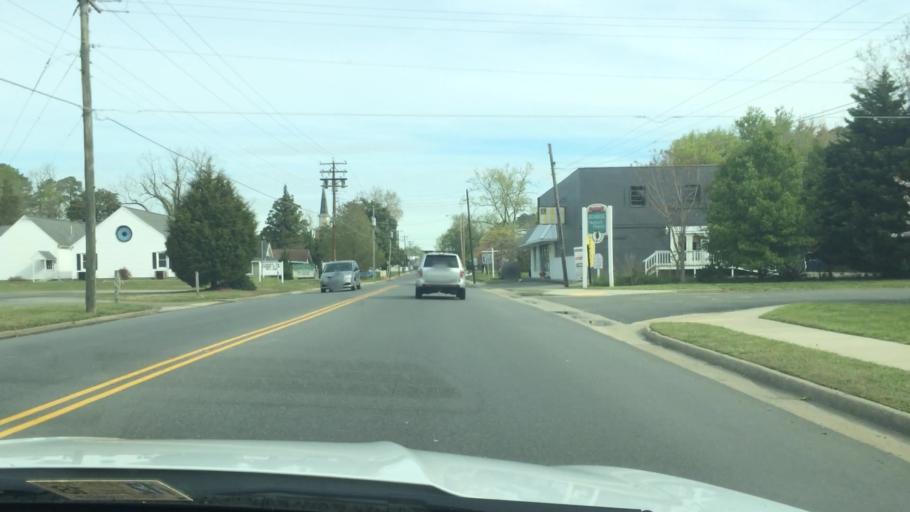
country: US
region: Virginia
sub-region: Lancaster County
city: Kilmarnock
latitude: 37.7046
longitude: -76.3783
